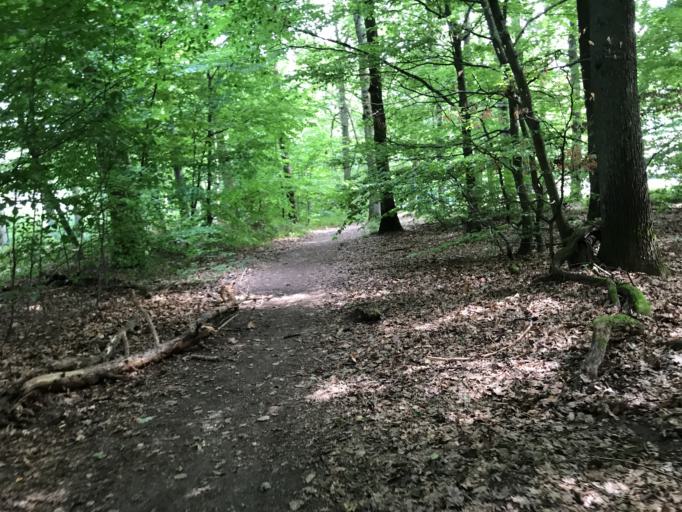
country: DE
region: Hesse
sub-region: Regierungsbezirk Darmstadt
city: Walluf
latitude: 50.0723
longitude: 8.1768
